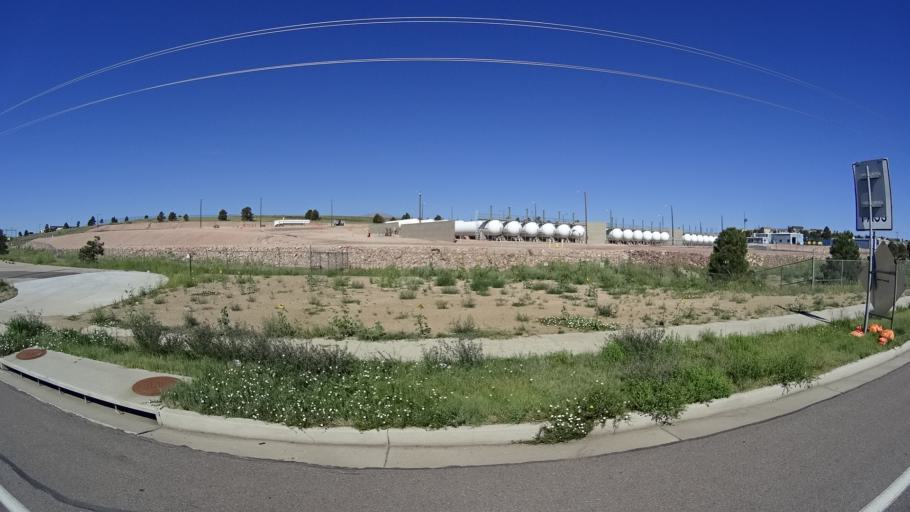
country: US
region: Colorado
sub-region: El Paso County
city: Cimarron Hills
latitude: 38.8846
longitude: -104.6829
